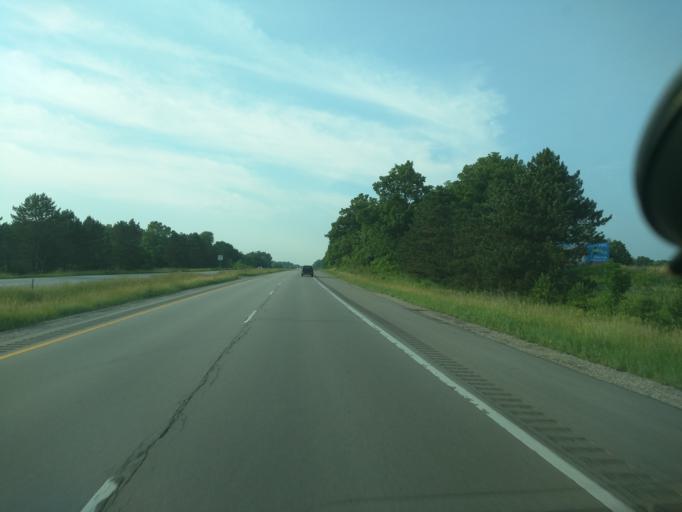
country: US
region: Michigan
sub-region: Ingham County
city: Leslie
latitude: 42.4405
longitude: -84.4434
